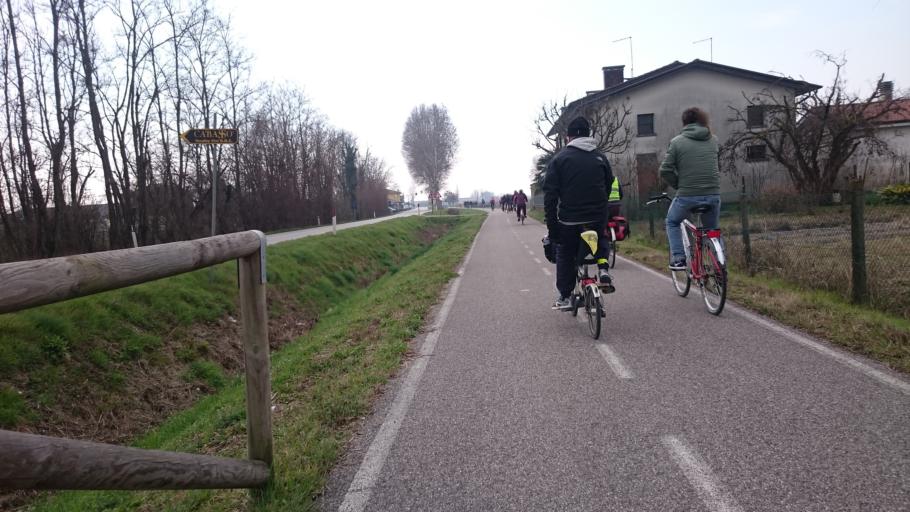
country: IT
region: Veneto
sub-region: Provincia di Vicenza
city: Lumignano
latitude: 45.4562
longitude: 11.6037
